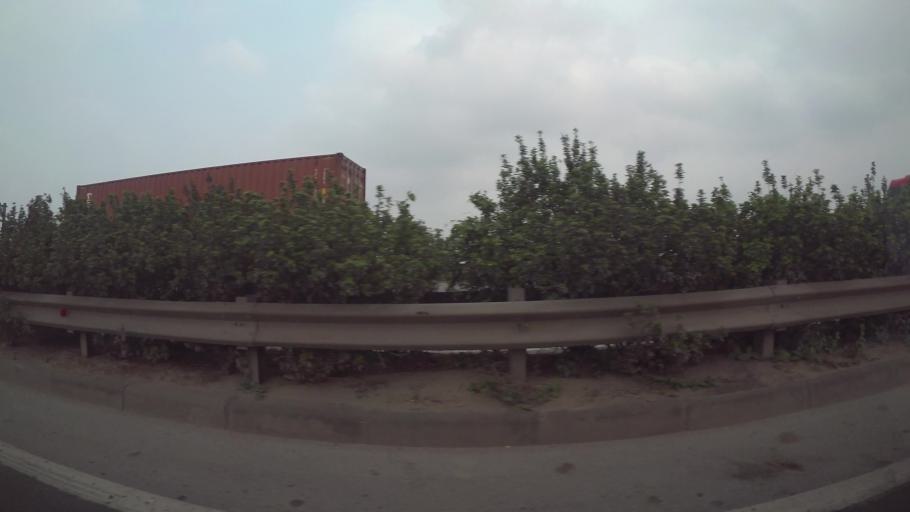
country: VN
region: Ha Noi
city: Trau Quy
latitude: 21.0211
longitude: 105.9266
